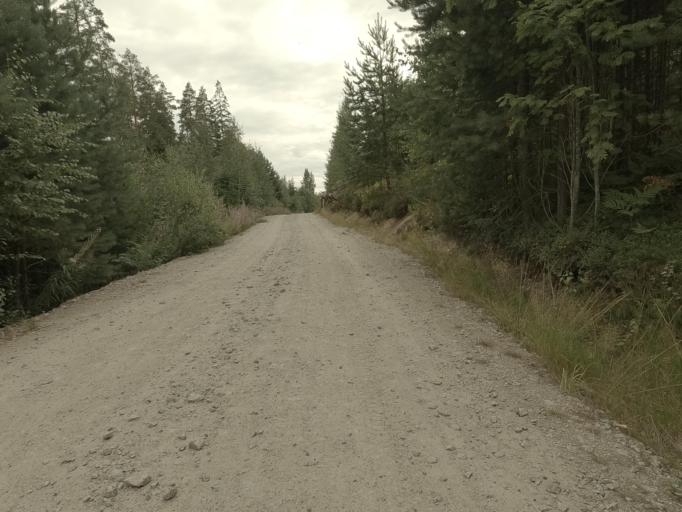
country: RU
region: Leningrad
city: Kamennogorsk
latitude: 60.9835
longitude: 29.1761
